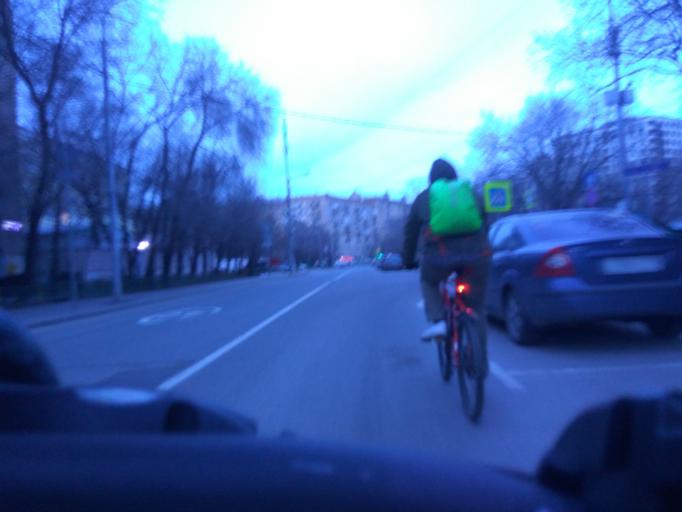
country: RU
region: Moskovskaya
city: Presnenskiy
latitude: 55.7432
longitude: 37.5507
